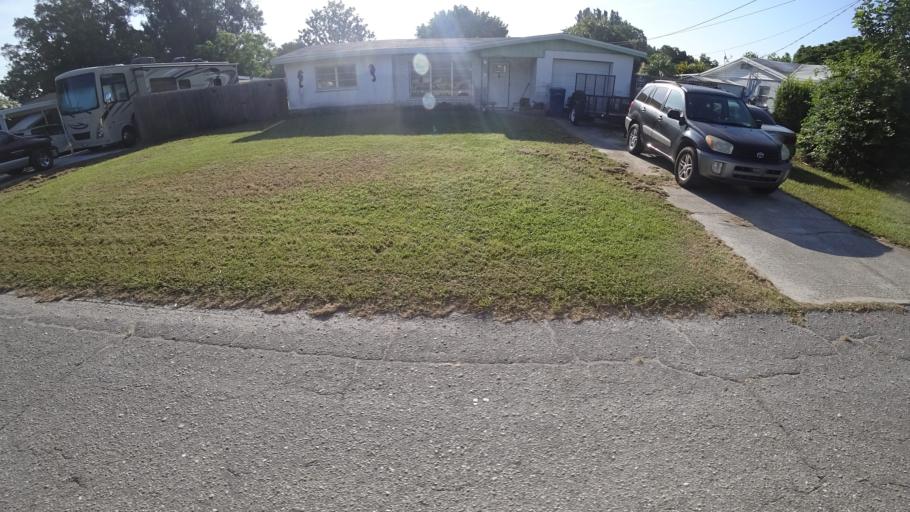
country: US
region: Florida
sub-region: Manatee County
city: South Bradenton
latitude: 27.4468
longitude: -82.5708
